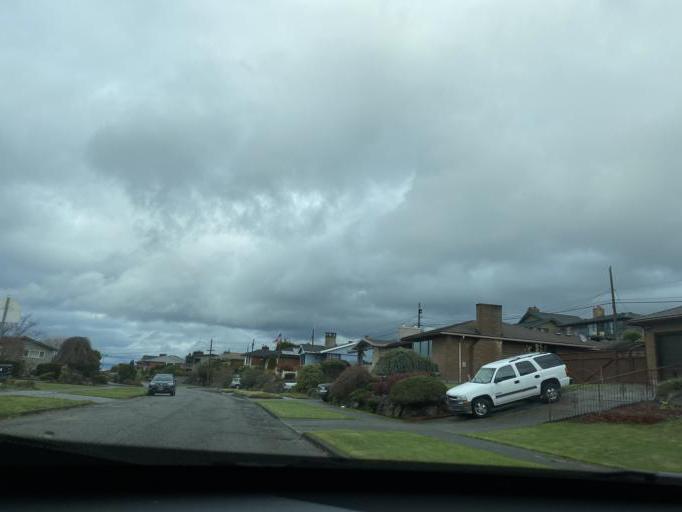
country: US
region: Washington
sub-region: King County
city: Shoreline
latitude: 47.6944
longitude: -122.3850
